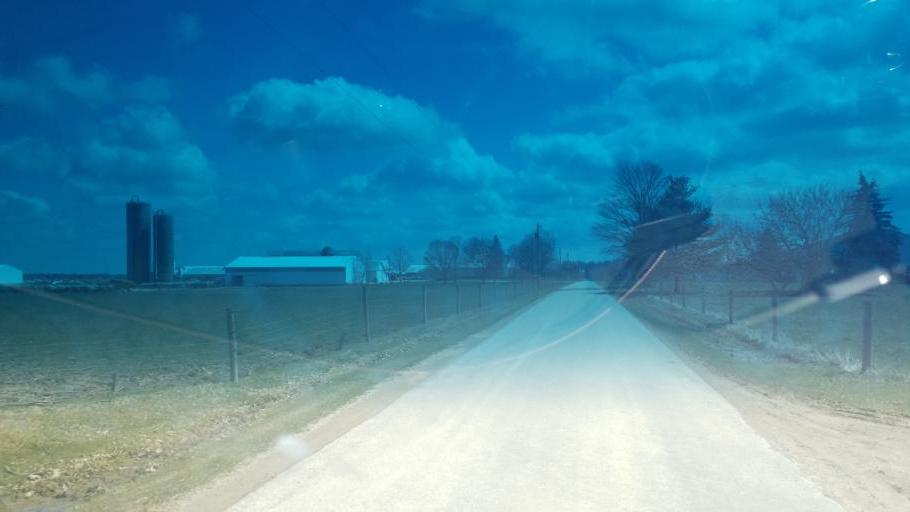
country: US
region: Ohio
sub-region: Crawford County
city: Bucyrus
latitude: 40.8487
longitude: -83.0023
